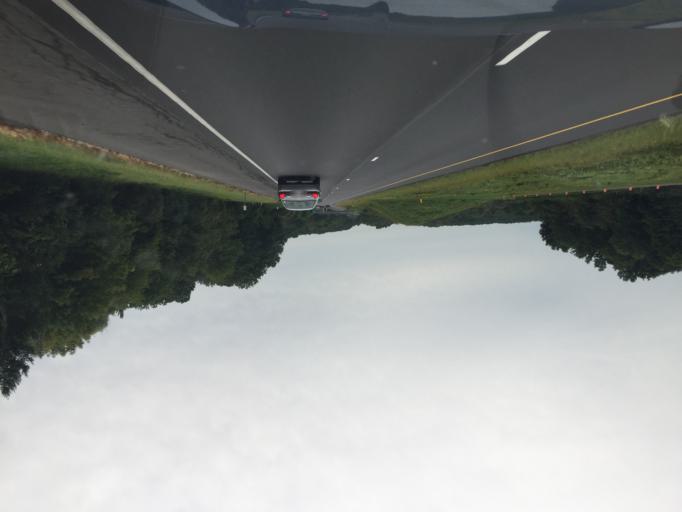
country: US
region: New York
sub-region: Rensselaer County
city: Nassau
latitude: 42.4840
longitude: -73.6401
